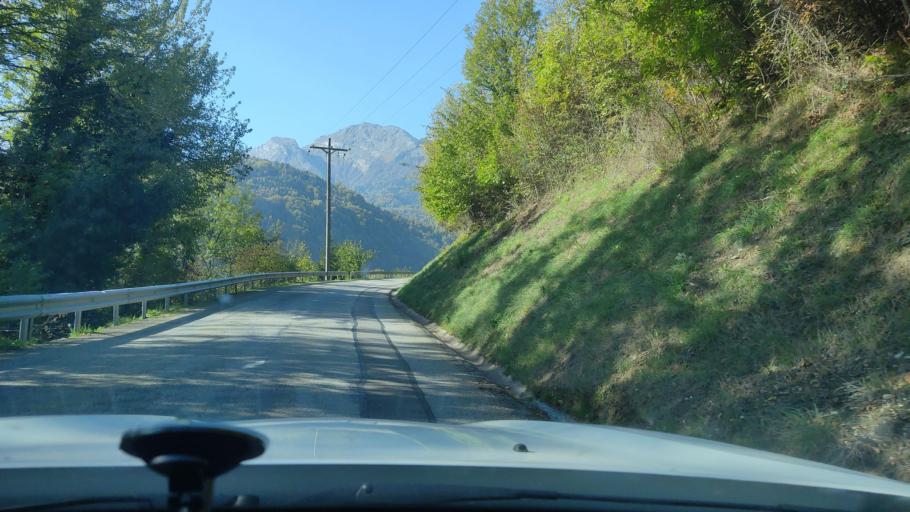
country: FR
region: Rhone-Alpes
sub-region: Departement de la Savoie
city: Ugine
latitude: 45.7486
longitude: 6.4299
